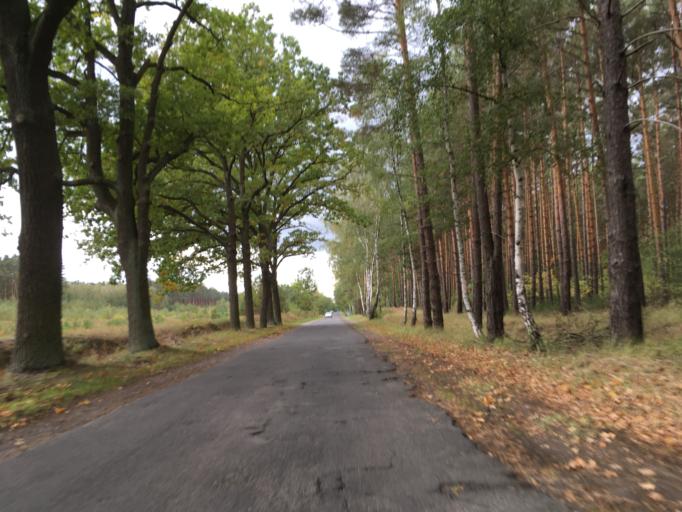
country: DE
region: Brandenburg
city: Birkenwerder
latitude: 52.6935
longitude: 13.3240
